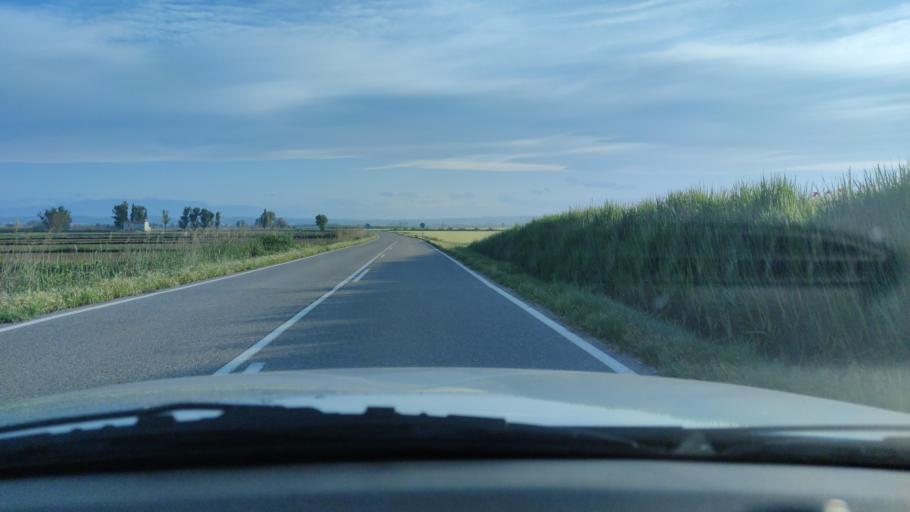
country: ES
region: Catalonia
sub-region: Provincia de Lleida
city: Ivars d'Urgell
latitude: 41.7045
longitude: 0.9818
